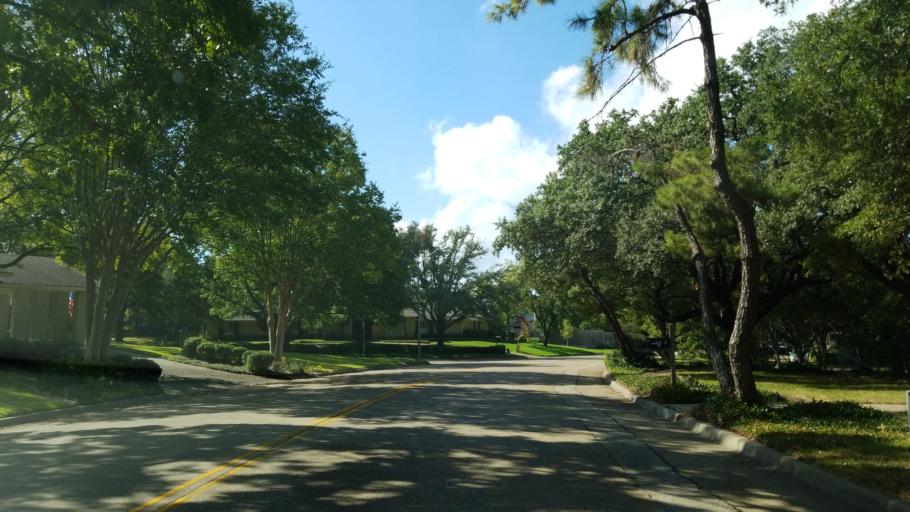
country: US
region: Texas
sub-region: Dallas County
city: Addison
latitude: 32.9491
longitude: -96.7925
